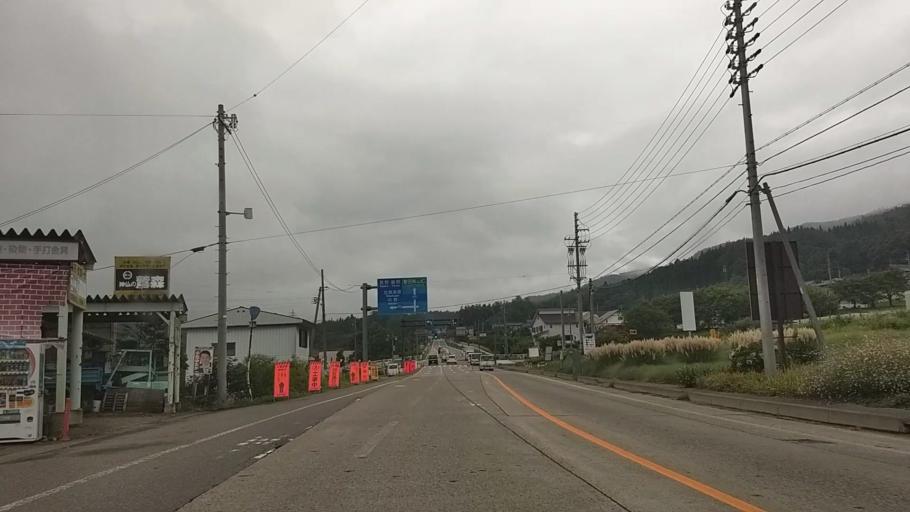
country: JP
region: Nagano
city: Iiyama
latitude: 36.8243
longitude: 138.3517
